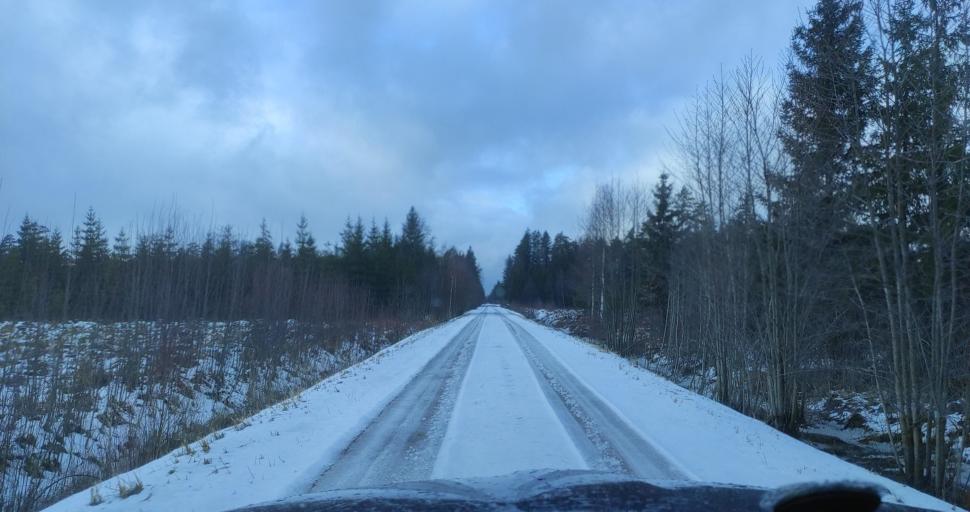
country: LV
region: Dundaga
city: Dundaga
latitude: 57.4095
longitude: 22.0852
